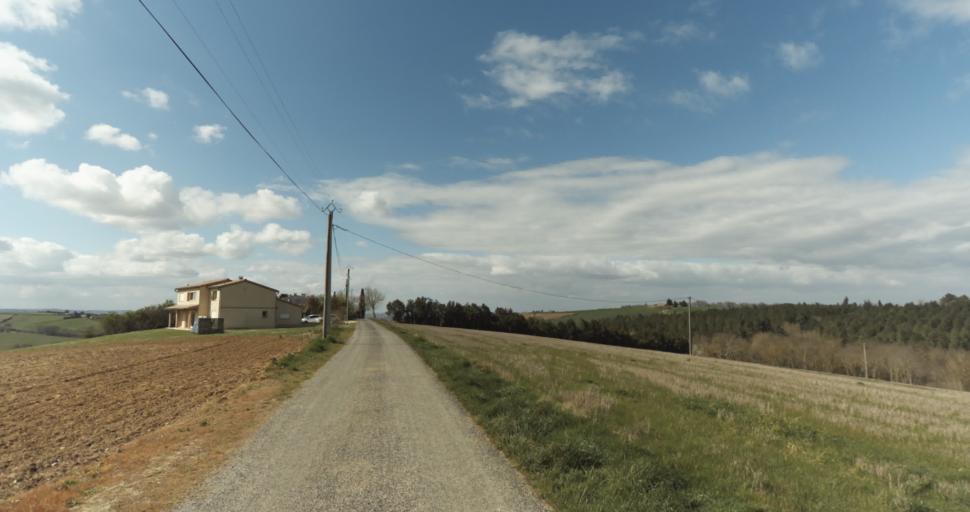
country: FR
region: Midi-Pyrenees
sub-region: Departement de la Haute-Garonne
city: Auterive
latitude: 43.3683
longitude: 1.5058
